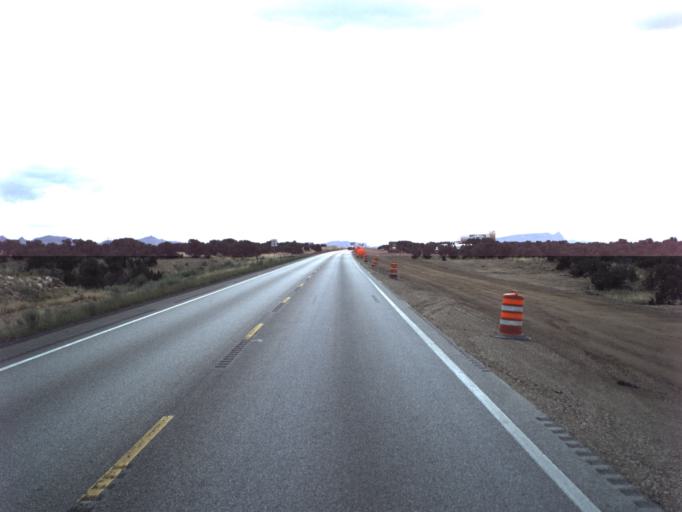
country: US
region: Utah
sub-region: Carbon County
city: East Carbon City
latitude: 39.4224
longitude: -110.4431
